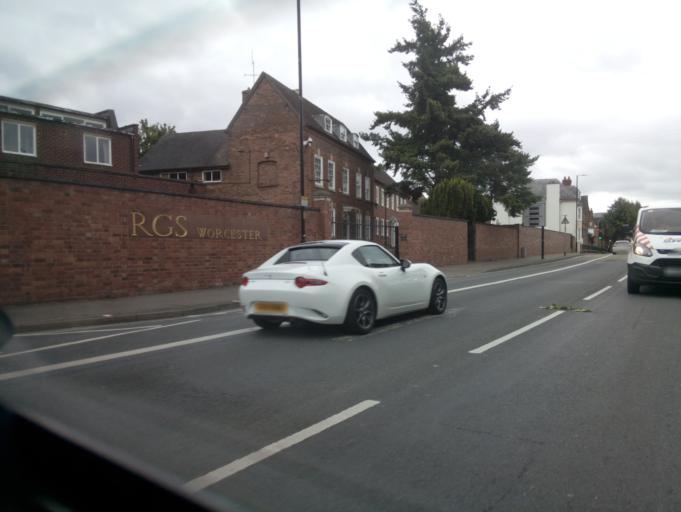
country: GB
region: England
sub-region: Worcestershire
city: Worcester
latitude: 52.2003
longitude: -2.2250
